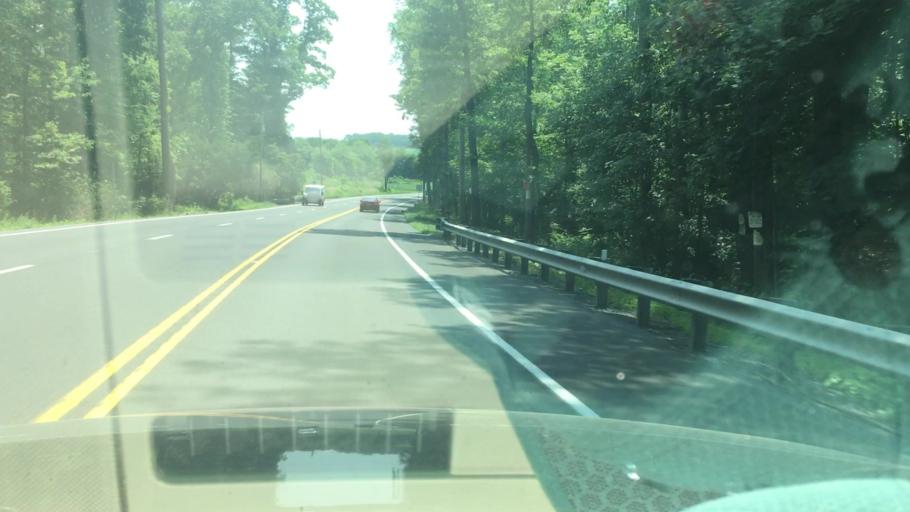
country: US
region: Pennsylvania
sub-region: Carbon County
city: Lehighton
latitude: 40.7161
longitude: -75.7689
